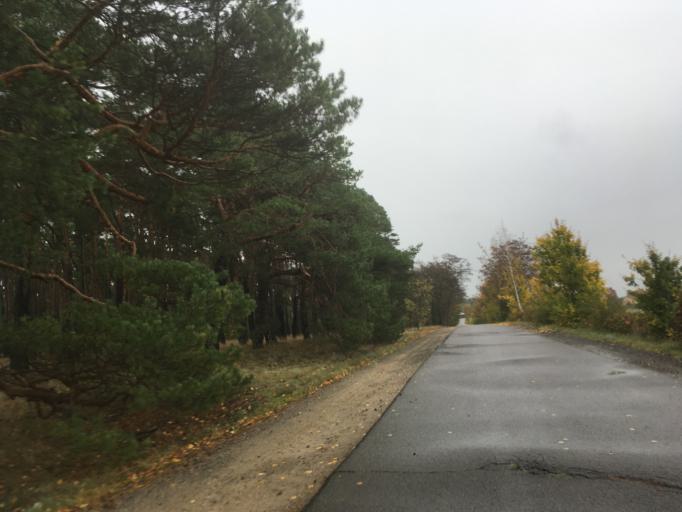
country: DE
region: Brandenburg
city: Neu Zauche
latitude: 52.0212
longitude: 14.1359
